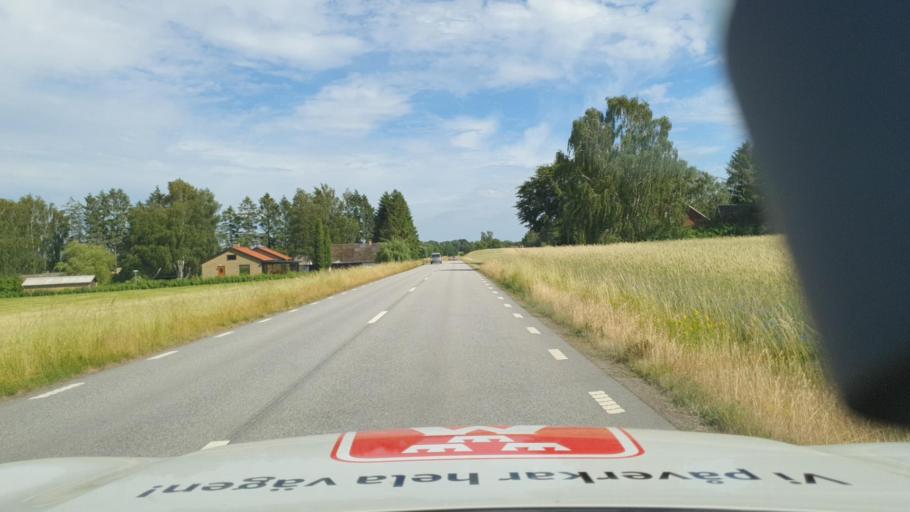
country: SE
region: Skane
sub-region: Sjobo Kommun
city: Blentarp
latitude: 55.6048
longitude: 13.5848
